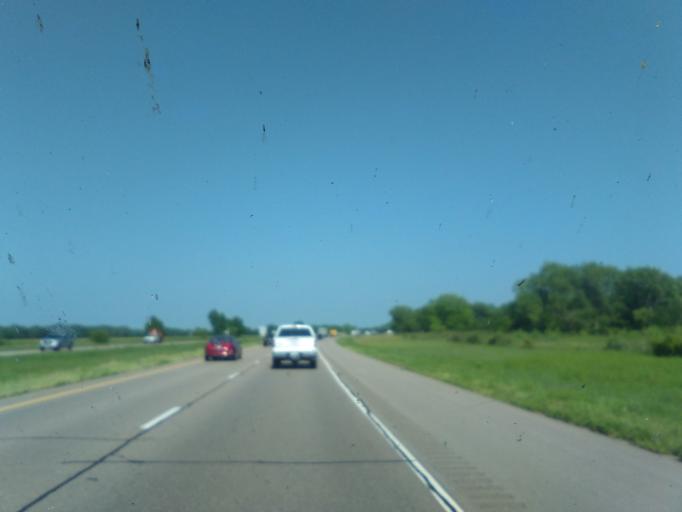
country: US
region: Nebraska
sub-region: Buffalo County
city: Gibbon
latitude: 40.6907
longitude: -98.9337
